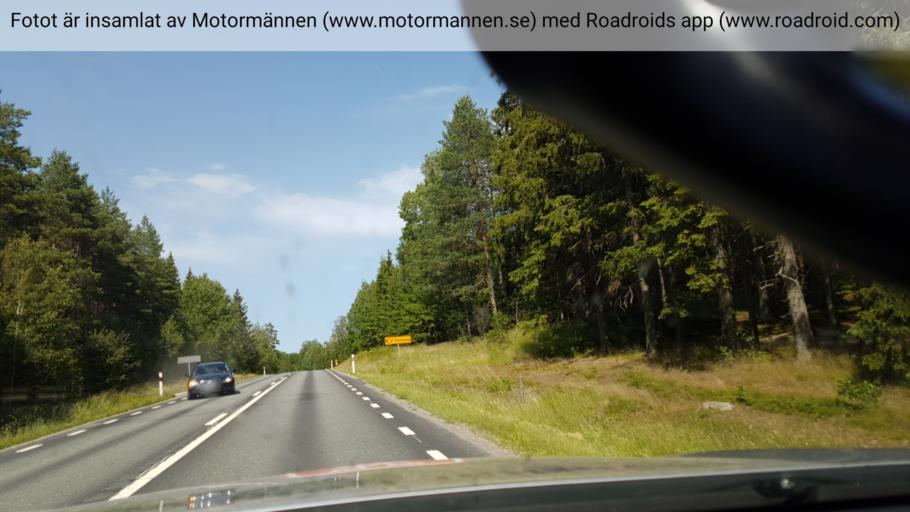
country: SE
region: Joenkoeping
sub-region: Aneby Kommun
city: Aneby
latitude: 57.9054
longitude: 14.8947
